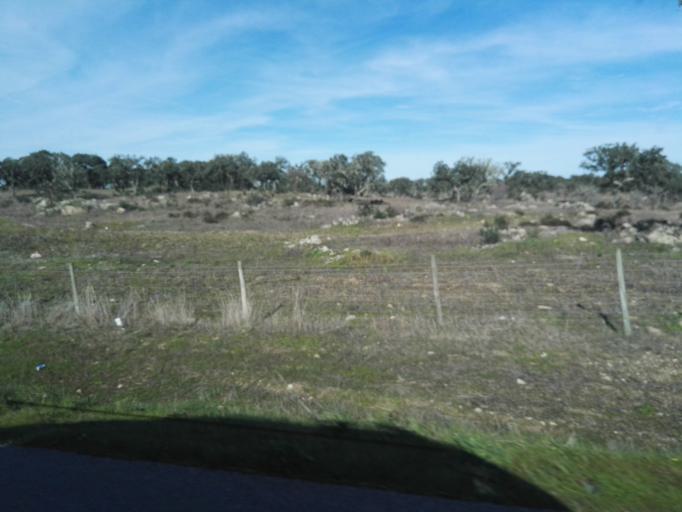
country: PT
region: Evora
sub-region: Arraiolos
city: Arraiolos
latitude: 38.8536
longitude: -7.9069
